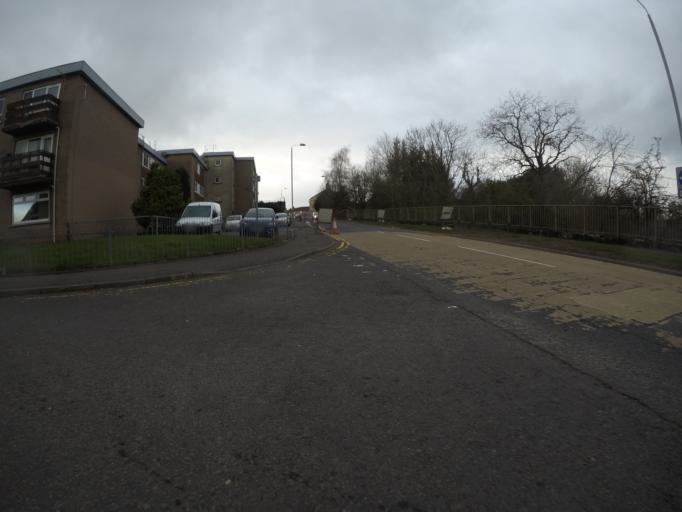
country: GB
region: Scotland
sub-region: East Ayrshire
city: Kilmarnock
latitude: 55.6146
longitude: -4.4930
